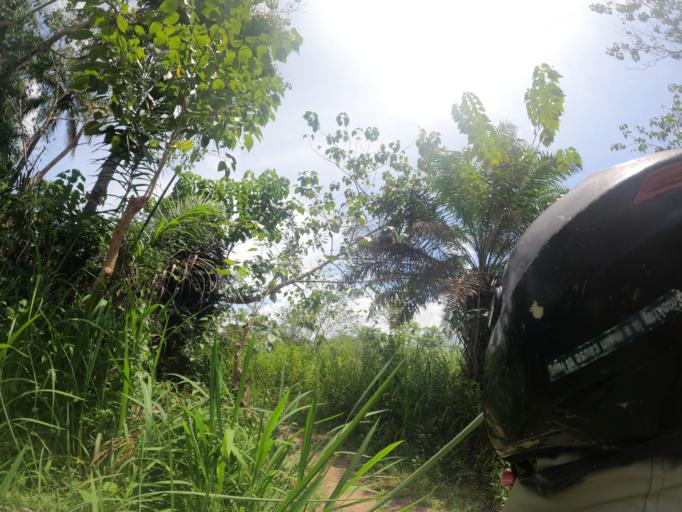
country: SL
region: Northern Province
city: Makeni
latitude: 9.1283
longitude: -12.2626
